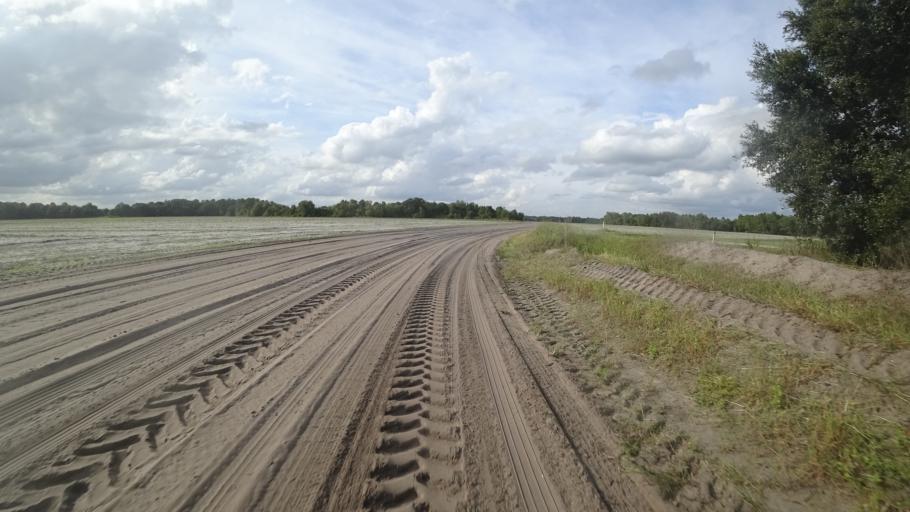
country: US
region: Florida
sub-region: Hillsborough County
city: Wimauma
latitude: 27.6040
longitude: -82.1416
